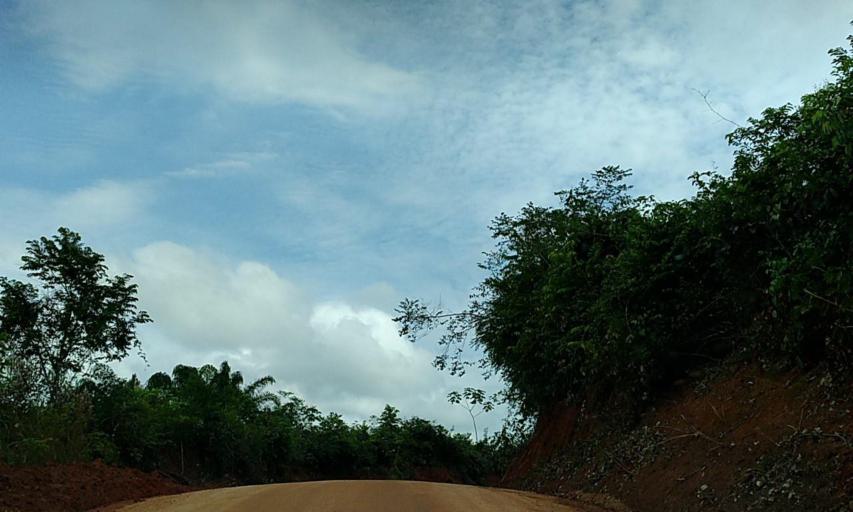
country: BR
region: Para
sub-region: Altamira
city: Altamira
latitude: -3.0817
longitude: -51.6348
